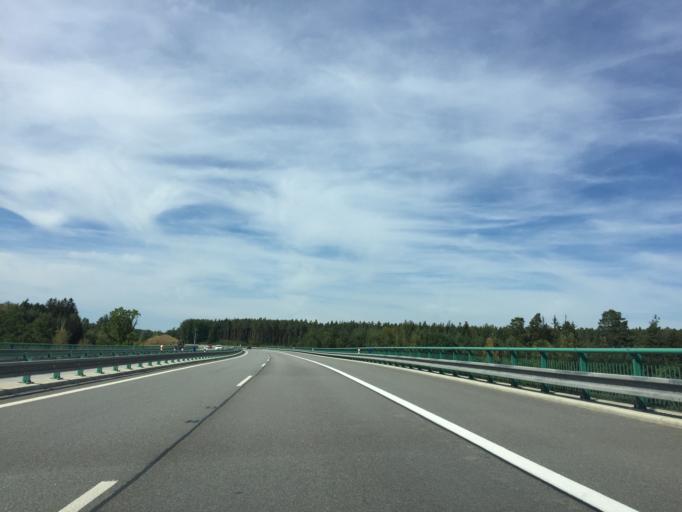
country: CZ
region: Jihocesky
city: Plana nad Luznici
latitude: 49.3366
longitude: 14.7375
